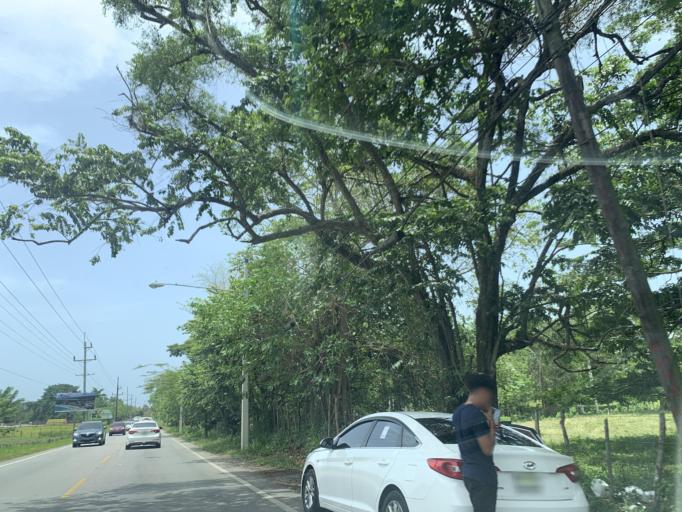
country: DO
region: Puerto Plata
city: Cabarete
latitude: 19.7766
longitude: -70.4881
